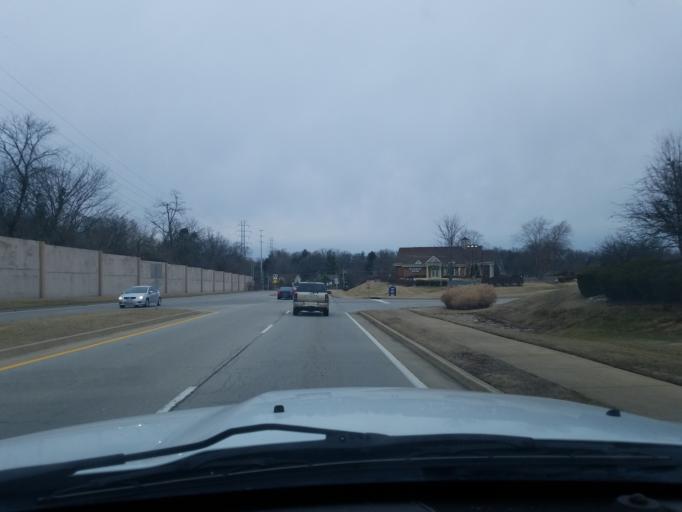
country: US
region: Kentucky
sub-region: Jefferson County
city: Douglass Hills
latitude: 38.2421
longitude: -85.5464
